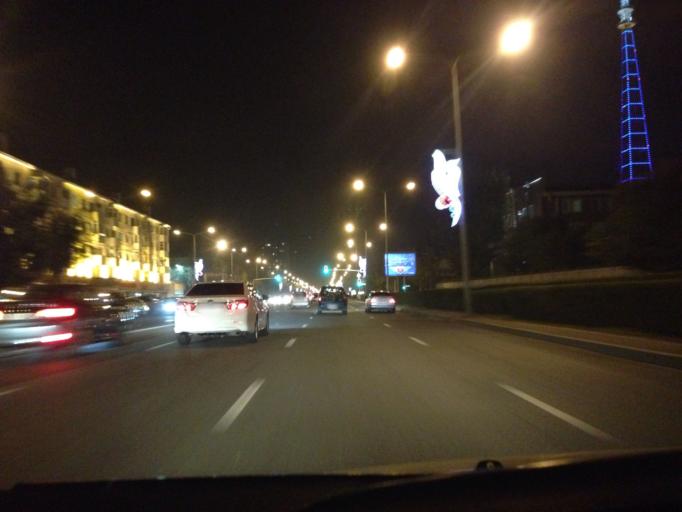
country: KZ
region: Astana Qalasy
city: Astana
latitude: 51.1803
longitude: 71.4099
